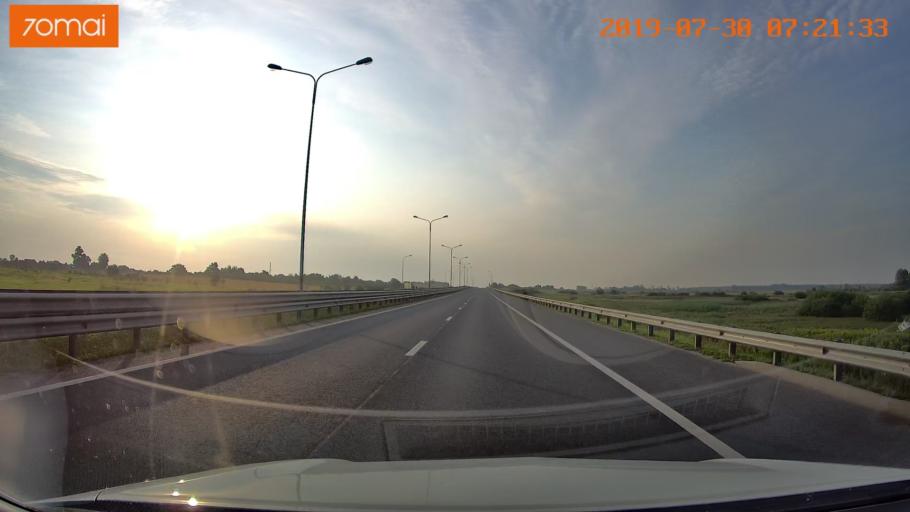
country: RU
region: Kaliningrad
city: Bol'shoe Isakovo
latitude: 54.6959
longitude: 20.7320
